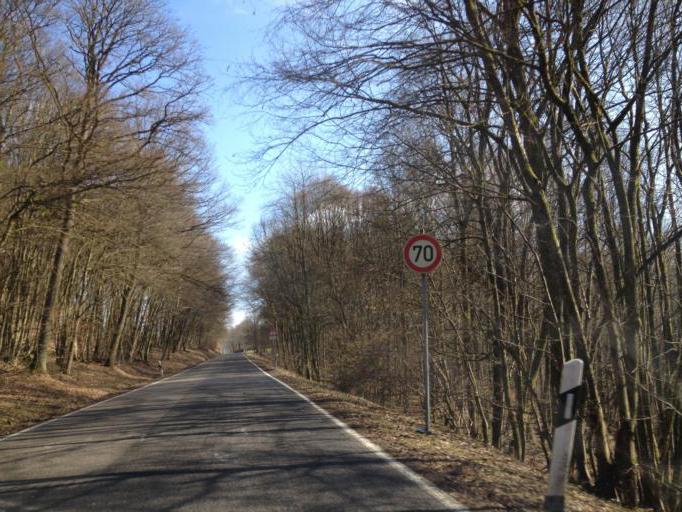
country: DE
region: Saarland
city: Sankt Wendel
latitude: 49.4694
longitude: 7.2228
